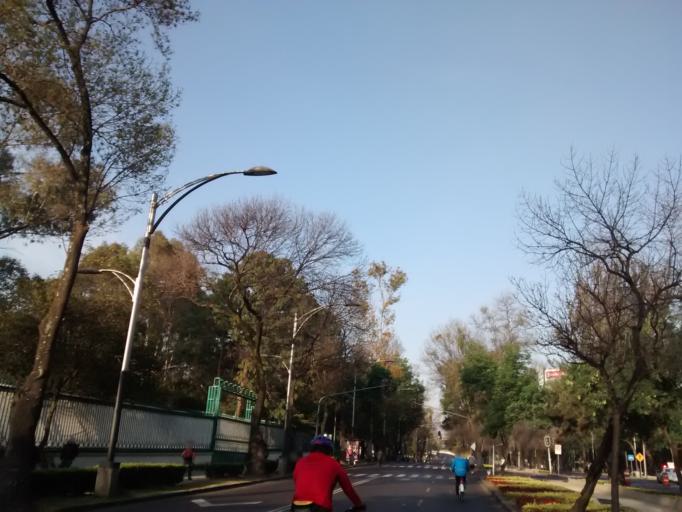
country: MX
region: Mexico City
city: Miguel Hidalgo
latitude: 19.4265
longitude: -99.1969
